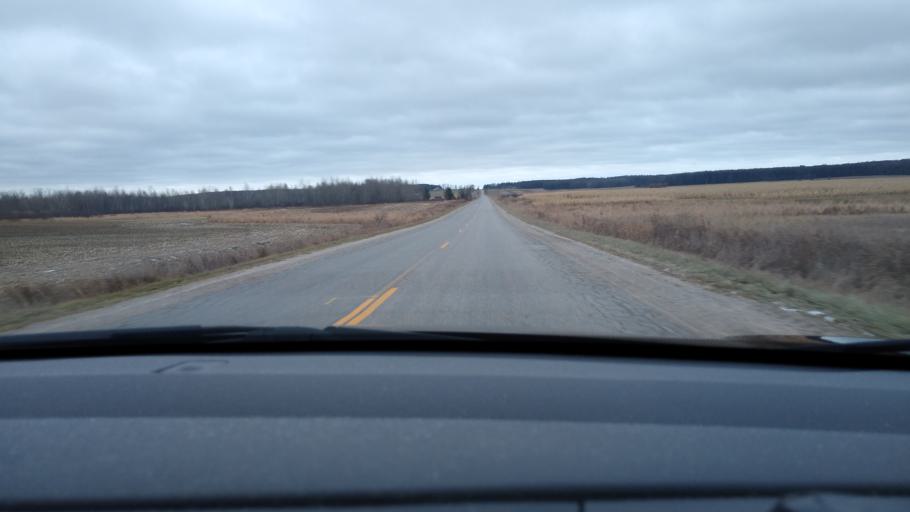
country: US
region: Michigan
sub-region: Missaukee County
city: Lake City
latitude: 44.3012
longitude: -85.0544
